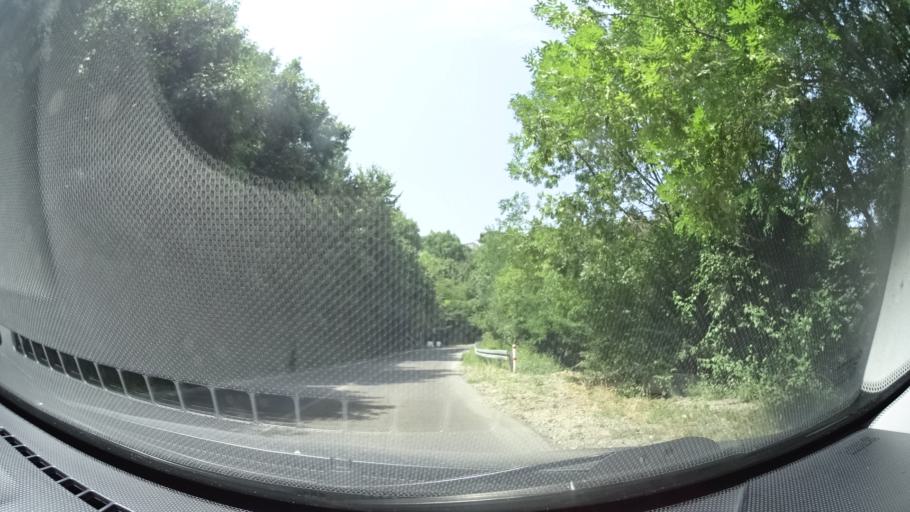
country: GE
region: Kakheti
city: Sighnaghi
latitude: 41.6223
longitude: 45.9264
